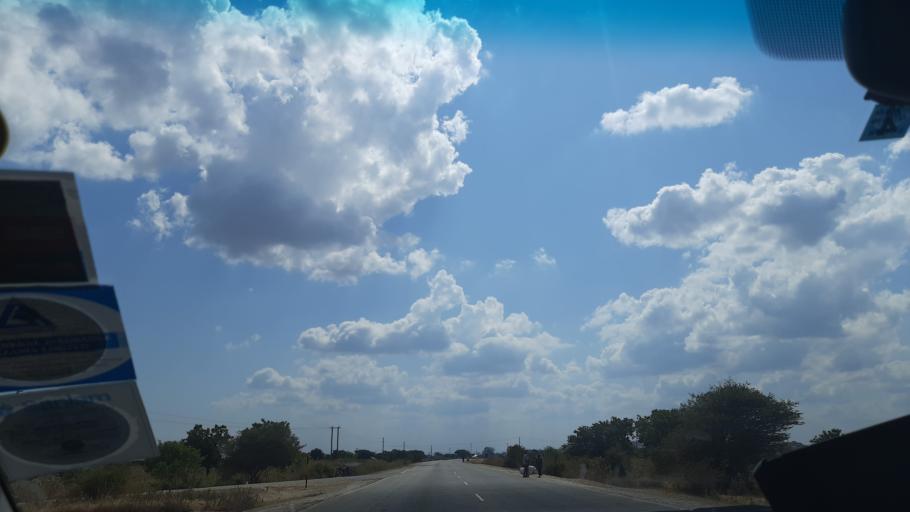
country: TZ
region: Singida
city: Kintinku
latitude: -5.9650
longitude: 35.3295
